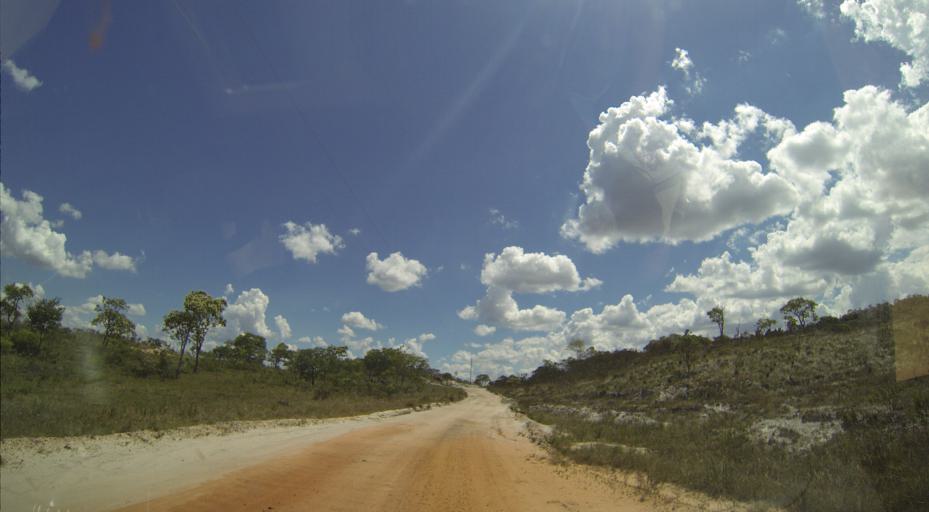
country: BR
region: Minas Gerais
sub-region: Serro
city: Serro
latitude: -18.4621
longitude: -43.4510
